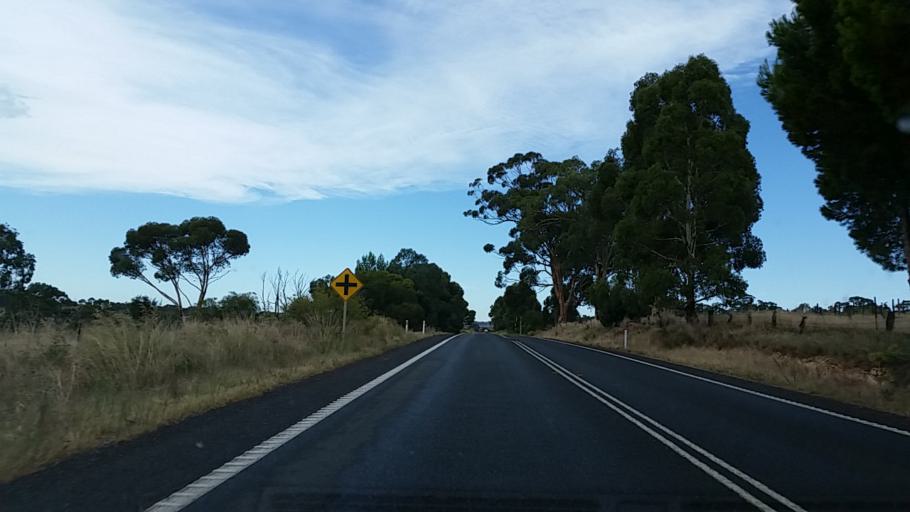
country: AU
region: South Australia
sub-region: Barossa
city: Tanunda
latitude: -34.5361
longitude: 138.9183
